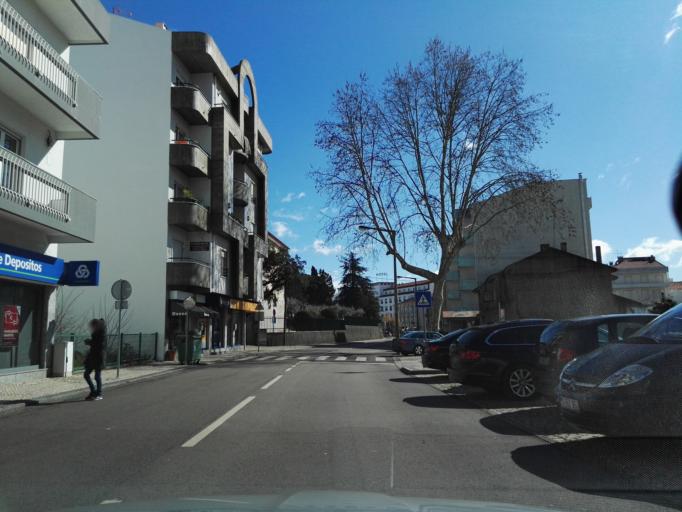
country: PT
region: Santarem
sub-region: Ourem
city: Fatima
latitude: 39.6330
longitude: -8.6799
